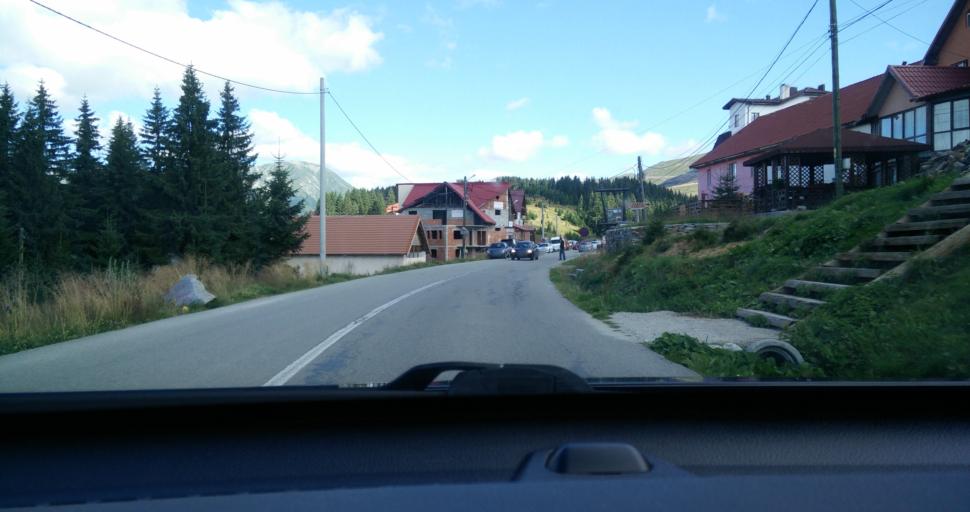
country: RO
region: Gorj
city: Novaci-Straini
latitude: 45.2900
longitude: 23.6895
